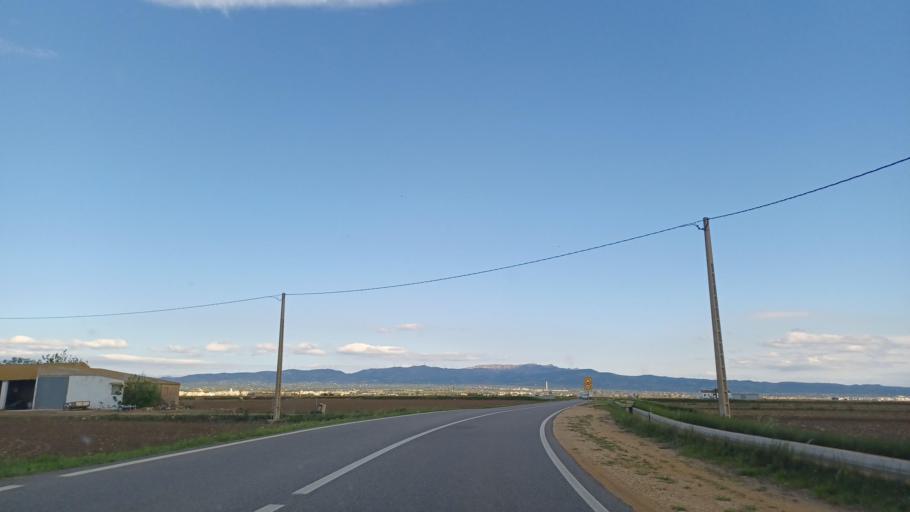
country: ES
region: Catalonia
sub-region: Provincia de Tarragona
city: Deltebre
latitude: 40.7512
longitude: 0.7056
